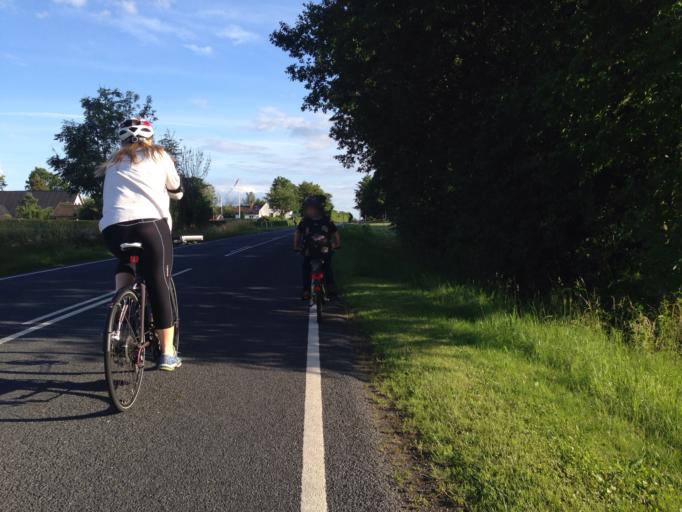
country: DK
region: South Denmark
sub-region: Middelfart Kommune
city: Norre Aby
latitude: 55.4828
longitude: 9.9020
